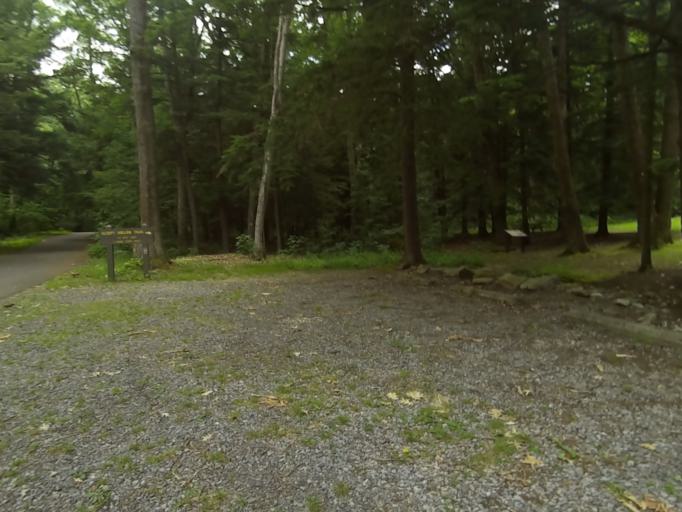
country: US
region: Pennsylvania
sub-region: Centre County
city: Stormstown
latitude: 40.9150
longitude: -78.0642
